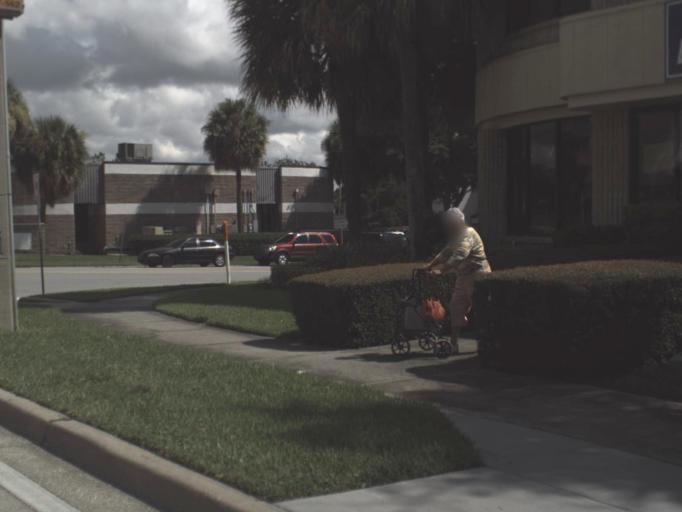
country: US
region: Florida
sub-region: Polk County
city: Lakeland
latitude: 28.0605
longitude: -81.9532
